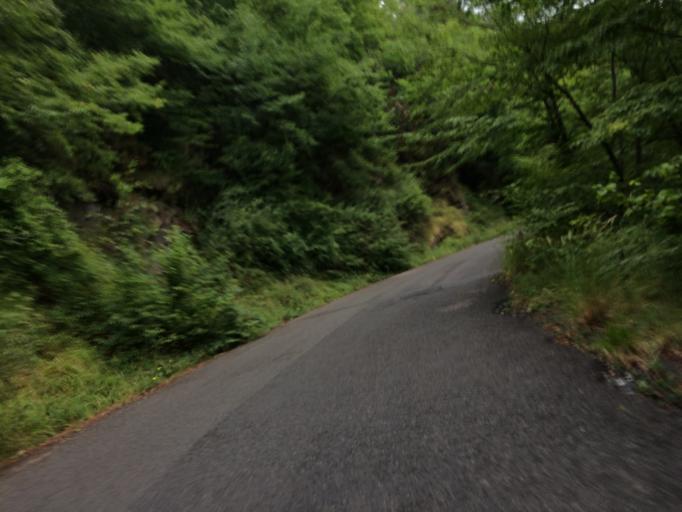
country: IT
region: Liguria
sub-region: Provincia di Imperia
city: Triora
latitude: 43.9784
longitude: 7.7466
